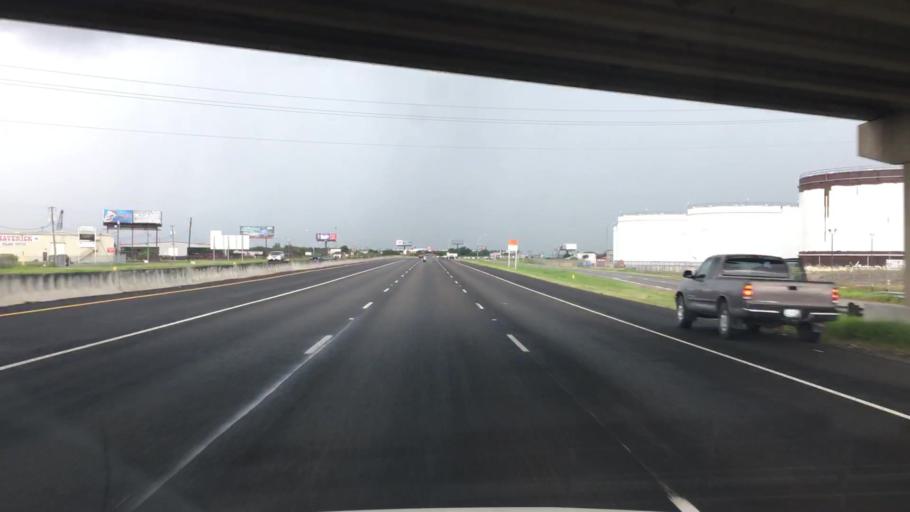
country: US
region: Texas
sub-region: Nueces County
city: Corpus Christi
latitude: 27.8113
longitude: -97.5026
